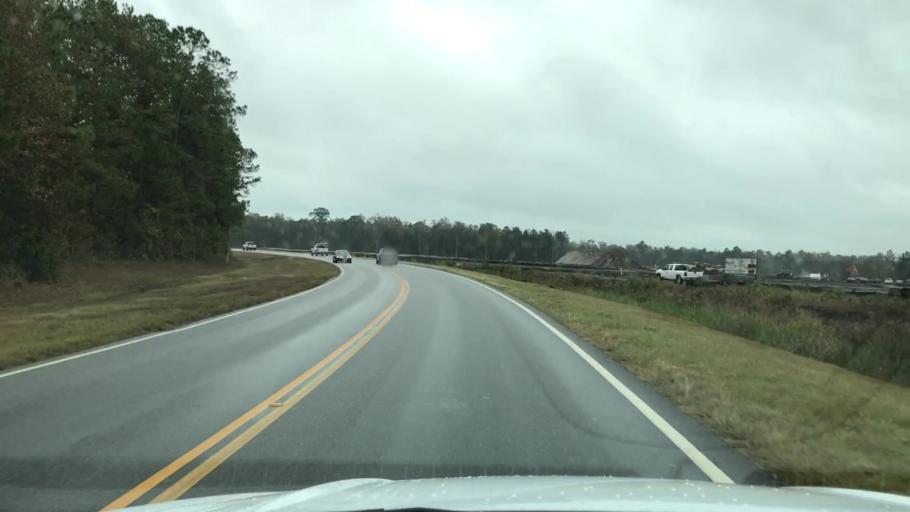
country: US
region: South Carolina
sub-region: Horry County
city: Myrtle Beach
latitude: 33.7555
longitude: -78.8827
